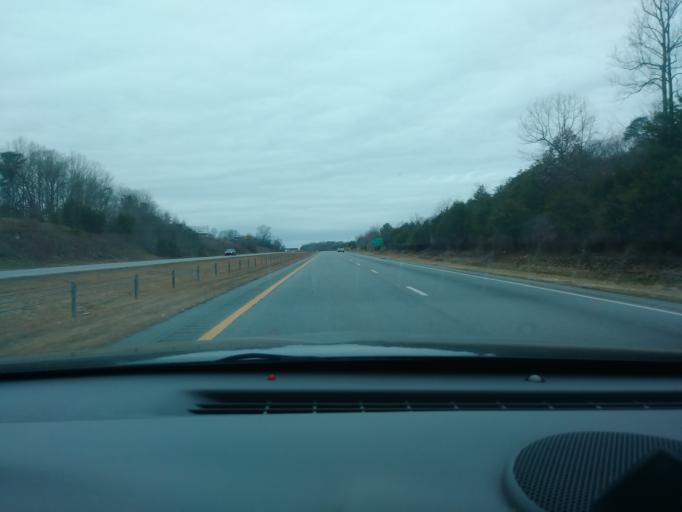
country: US
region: North Carolina
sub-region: Yadkin County
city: Yadkinville
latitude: 36.1198
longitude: -80.6879
